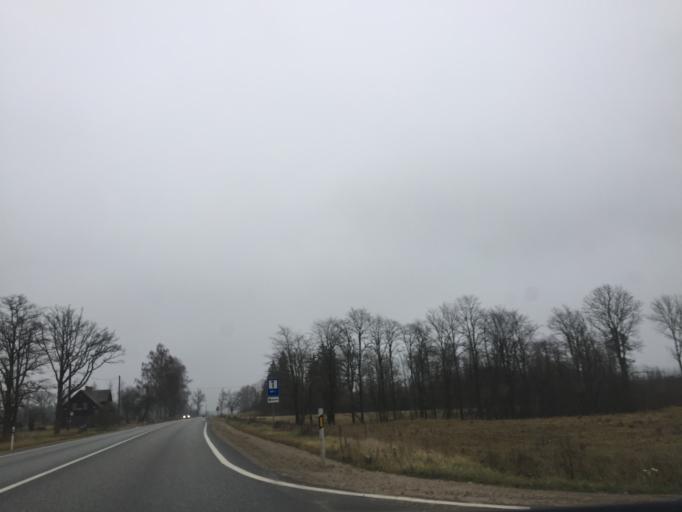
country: LV
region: Koceni
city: Koceni
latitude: 57.5145
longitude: 25.3442
